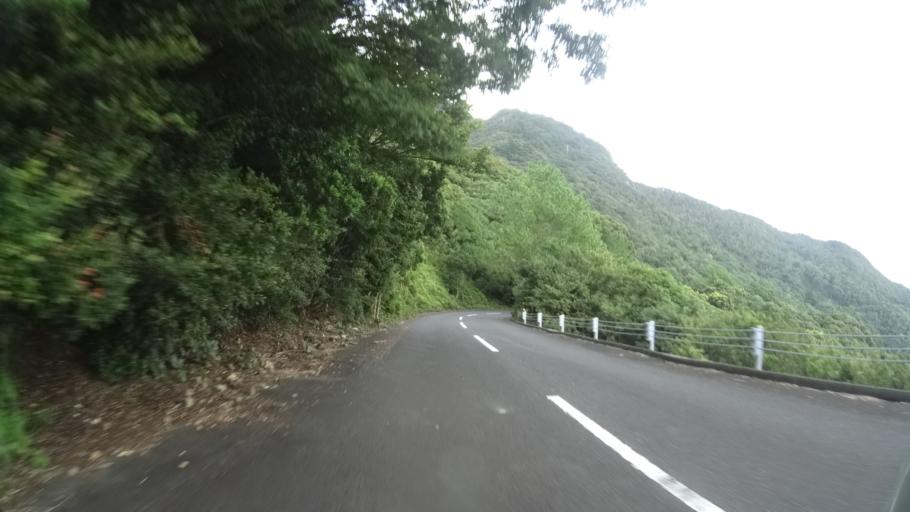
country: JP
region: Kagoshima
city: Nishinoomote
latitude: 30.3281
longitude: 130.3937
